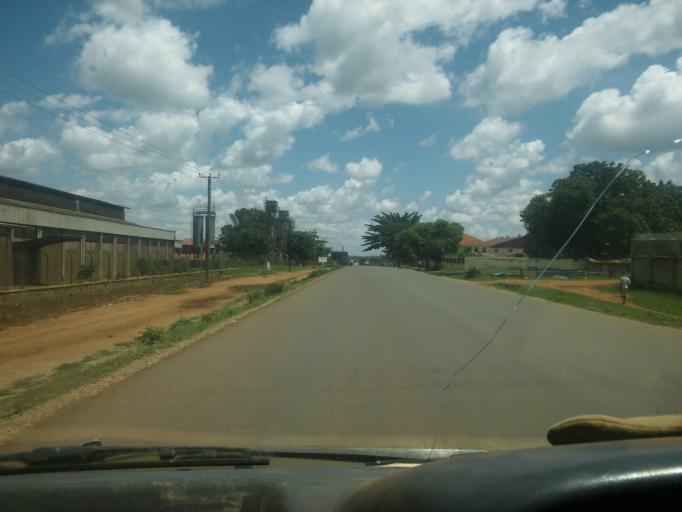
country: UG
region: Eastern Region
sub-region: Mbale District
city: Mbale
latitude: 1.0790
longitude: 34.1510
